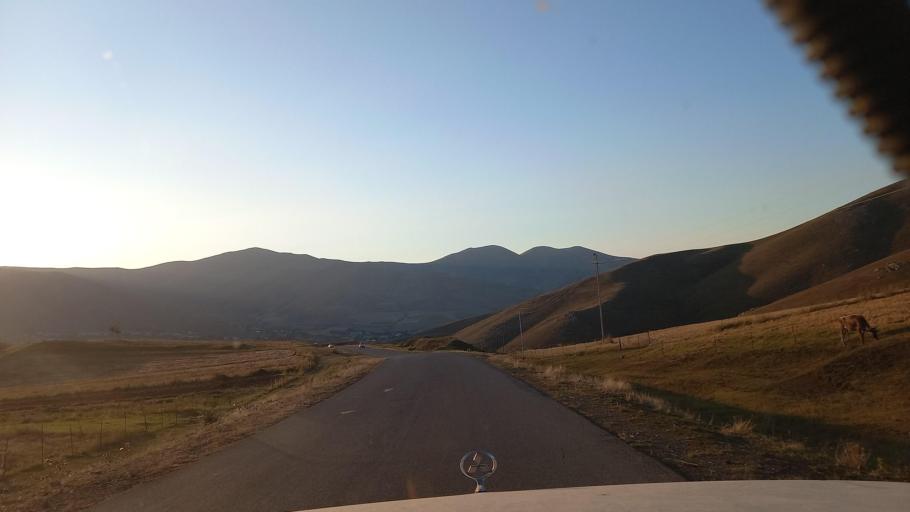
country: AZ
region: Gadabay Rayon
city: Ariqdam
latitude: 40.6819
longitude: 45.7793
